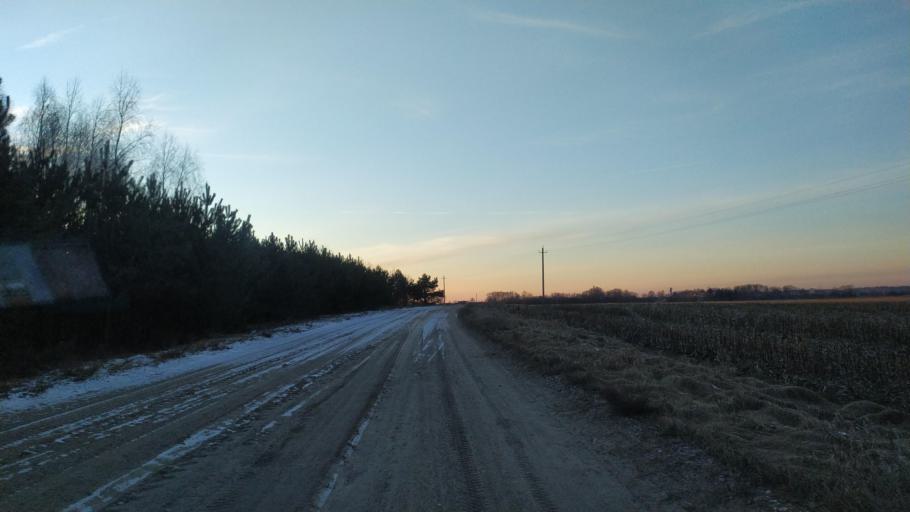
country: BY
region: Brest
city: Pruzhany
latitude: 52.5472
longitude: 24.2407
